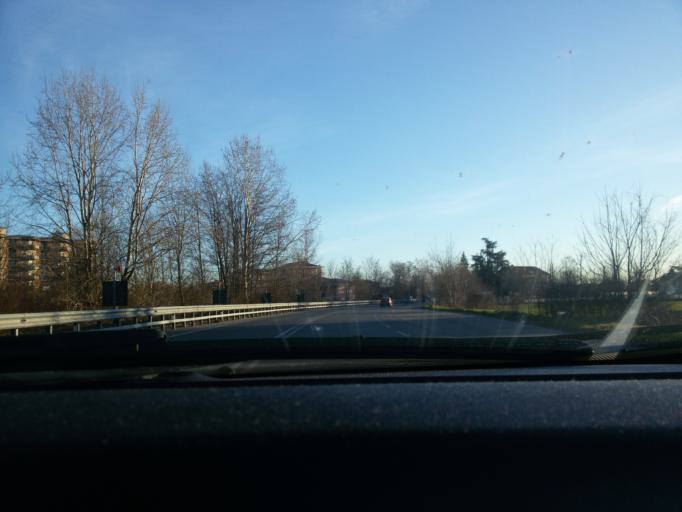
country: IT
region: Piedmont
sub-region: Provincia di Alessandria
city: Casale Monferrato
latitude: 45.1167
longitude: 8.4498
